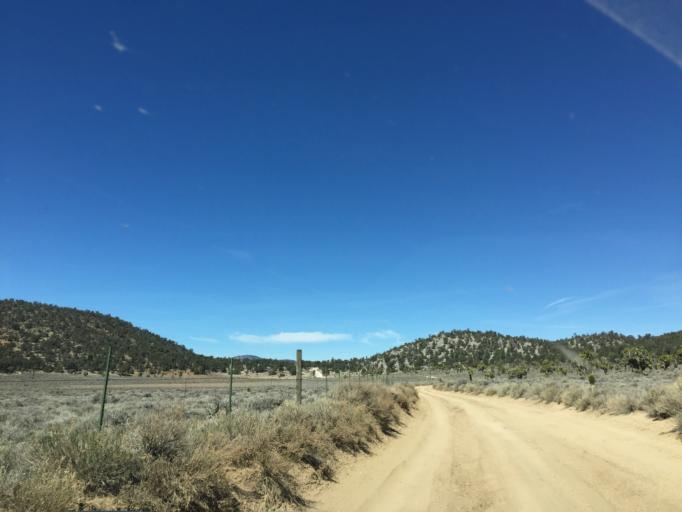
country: US
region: California
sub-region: San Bernardino County
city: Big Bear City
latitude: 34.2531
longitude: -116.7082
